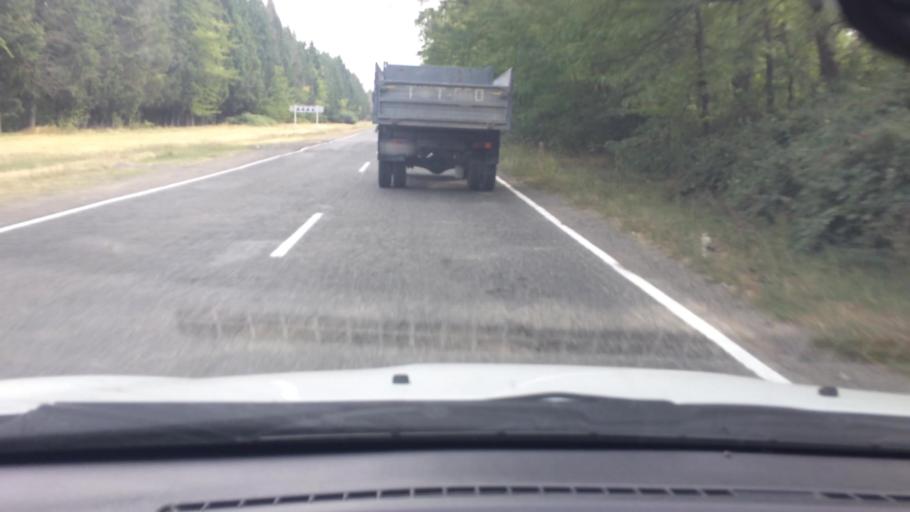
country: GE
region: Kvemo Kartli
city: Rust'avi
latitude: 41.4683
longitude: 44.9808
